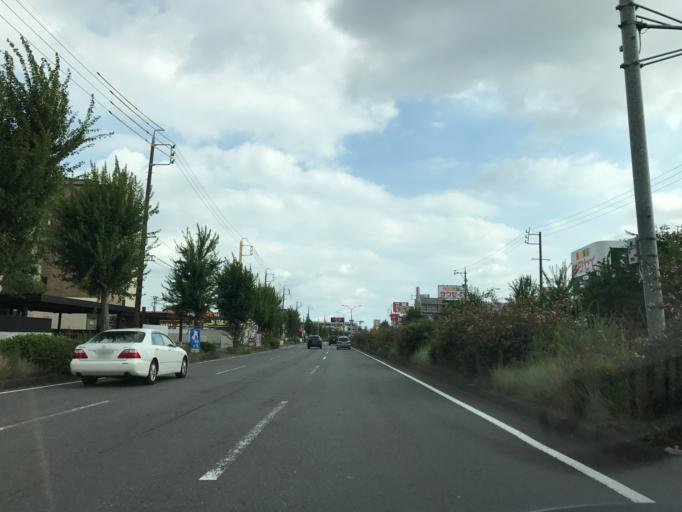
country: JP
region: Gifu
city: Gifu-shi
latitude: 35.3982
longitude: 136.7849
